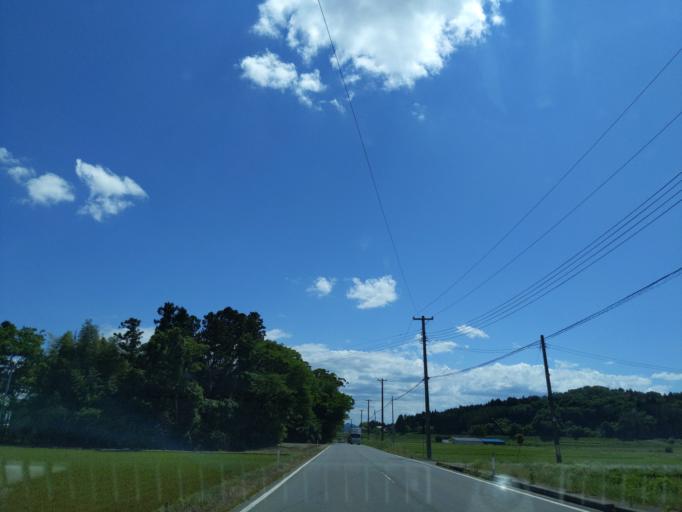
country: JP
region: Fukushima
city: Koriyama
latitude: 37.3804
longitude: 140.2966
